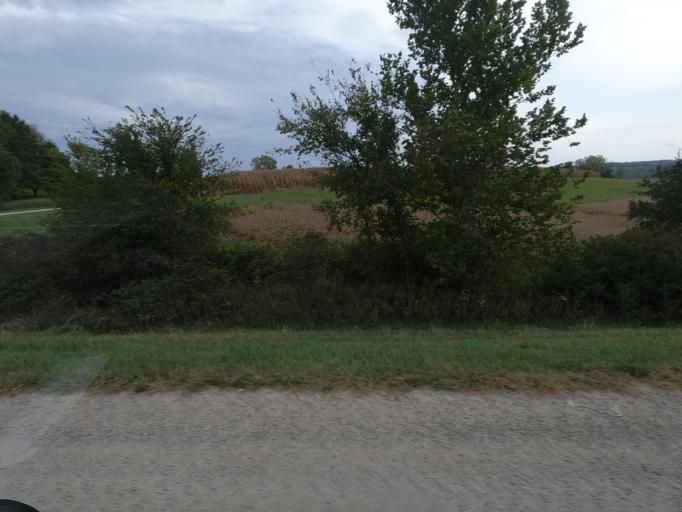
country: US
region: Iowa
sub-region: Van Buren County
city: Keosauqua
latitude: 40.8571
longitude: -92.1124
